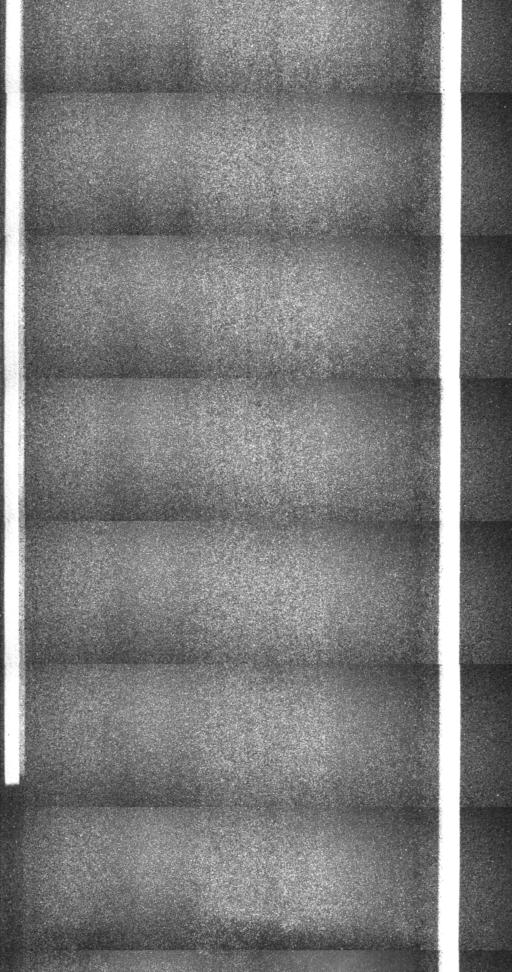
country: US
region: Vermont
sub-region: Windham County
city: Dover
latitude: 42.9679
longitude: -72.8871
